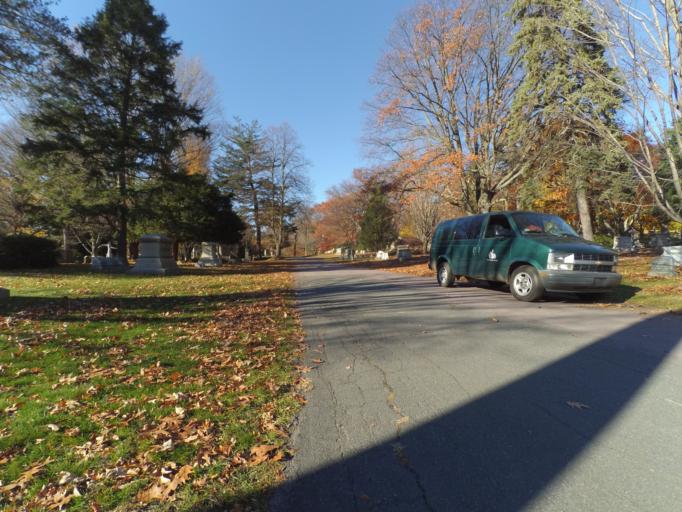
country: US
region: Massachusetts
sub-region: Middlesex County
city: Watertown
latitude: 42.3676
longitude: -71.1444
